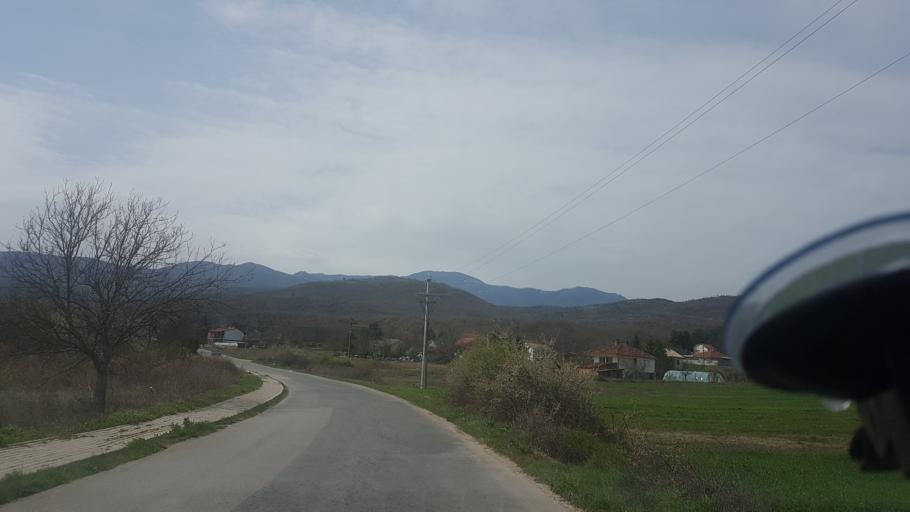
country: MK
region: Zelenikovo
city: Zelenikovo
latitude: 41.8924
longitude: 21.5899
